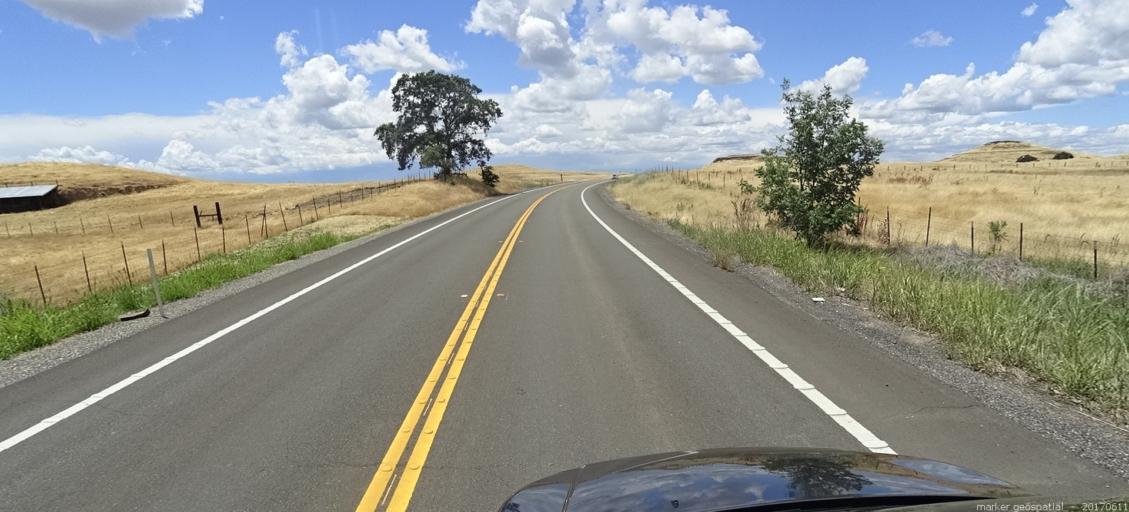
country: US
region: California
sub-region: Butte County
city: Paradise
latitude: 39.6397
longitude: -121.6656
